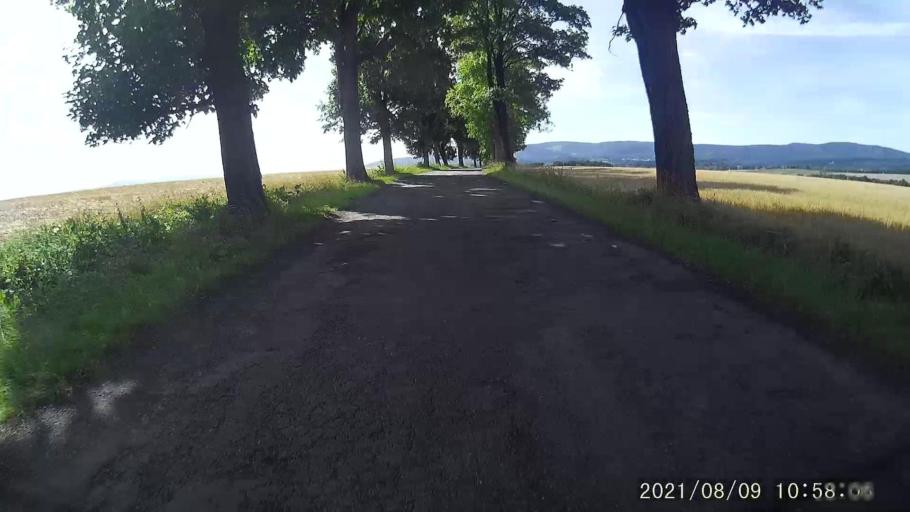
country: PL
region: Lower Silesian Voivodeship
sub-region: Powiat klodzki
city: Polanica-Zdroj
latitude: 50.4403
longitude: 16.5485
